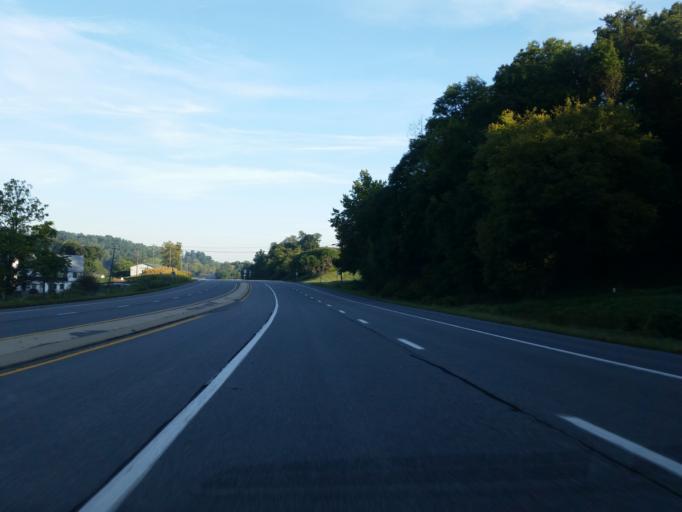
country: US
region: Pennsylvania
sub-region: Lancaster County
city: Willow Street
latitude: 39.9374
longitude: -76.2550
